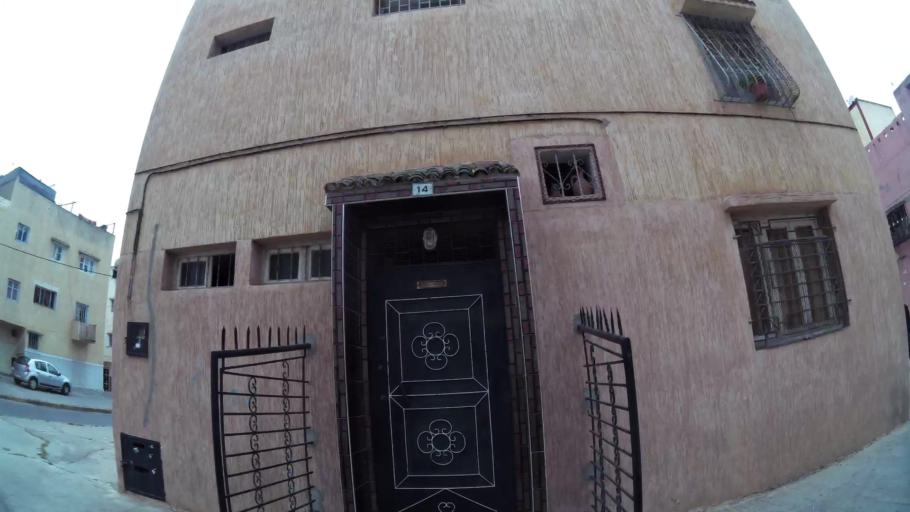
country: MA
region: Rabat-Sale-Zemmour-Zaer
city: Sale
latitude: 34.0483
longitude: -6.7993
